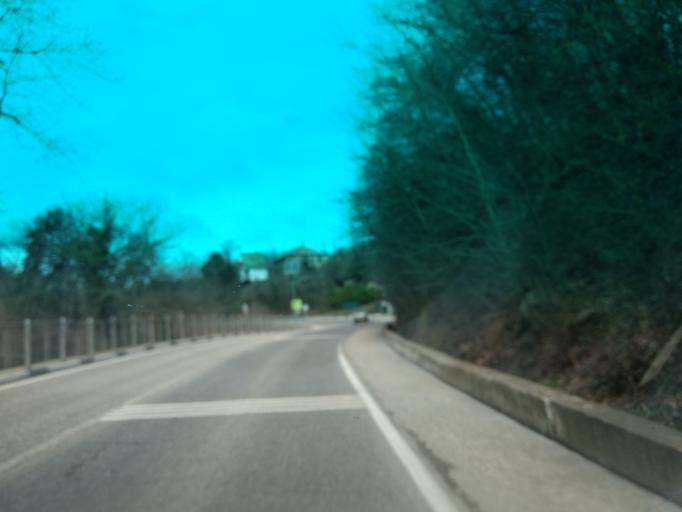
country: RU
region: Krasnodarskiy
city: Shepsi
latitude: 44.0412
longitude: 39.1420
